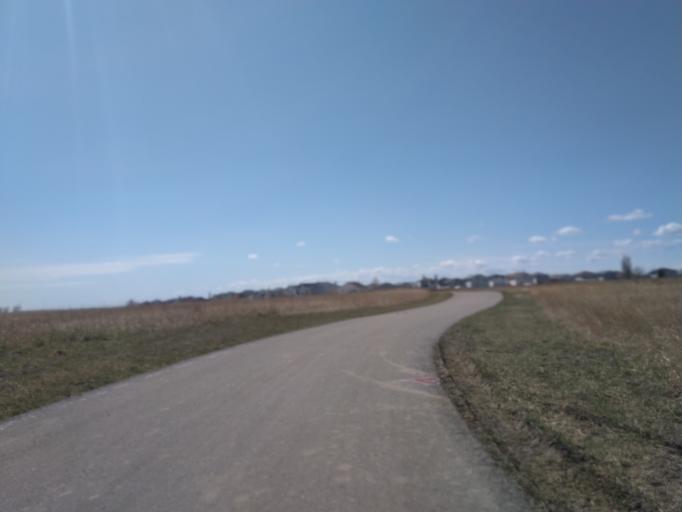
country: CA
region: Alberta
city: Chestermere
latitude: 51.0537
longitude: -113.9230
